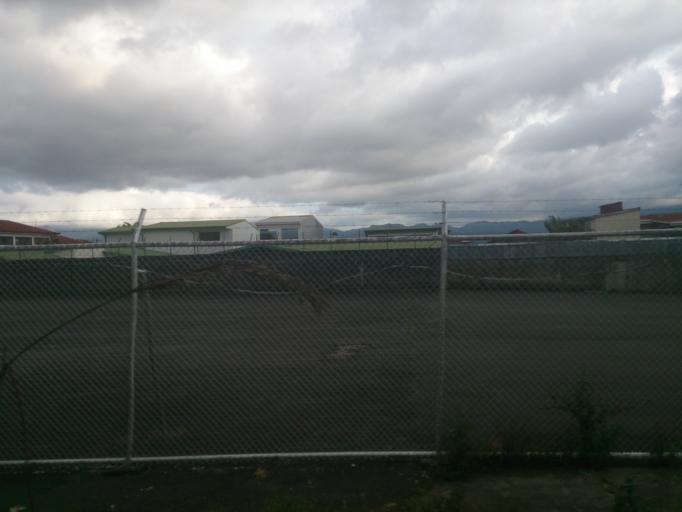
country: CR
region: San Jose
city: San Pedro
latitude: 9.9336
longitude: -84.0652
